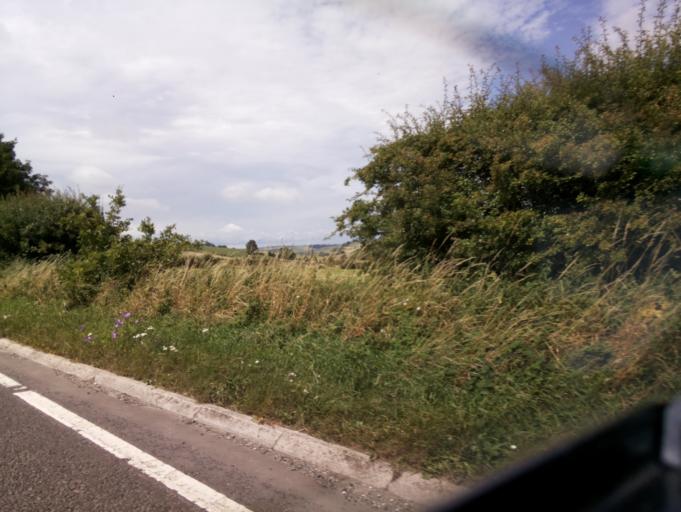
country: GB
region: England
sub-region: Dorset
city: Dorchester
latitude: 50.7587
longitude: -2.5245
